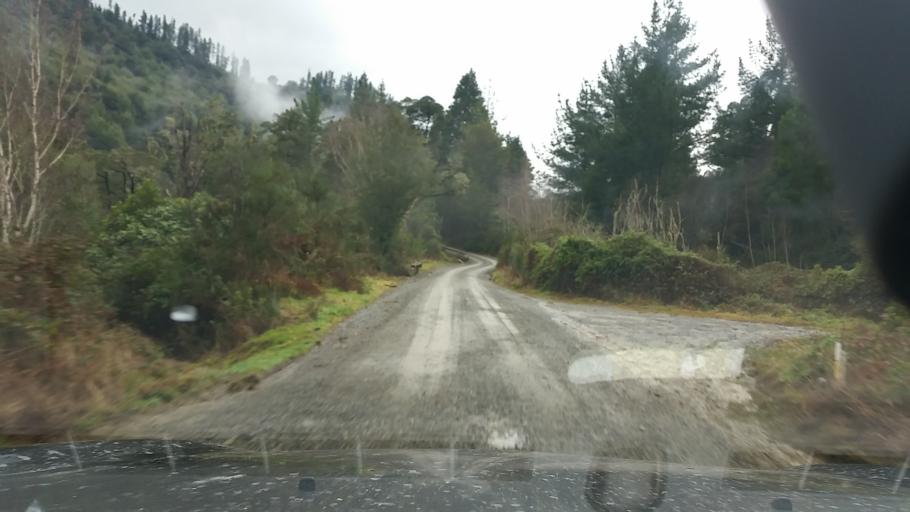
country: NZ
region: Nelson
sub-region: Nelson City
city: Nelson
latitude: -41.3590
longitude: 173.6200
